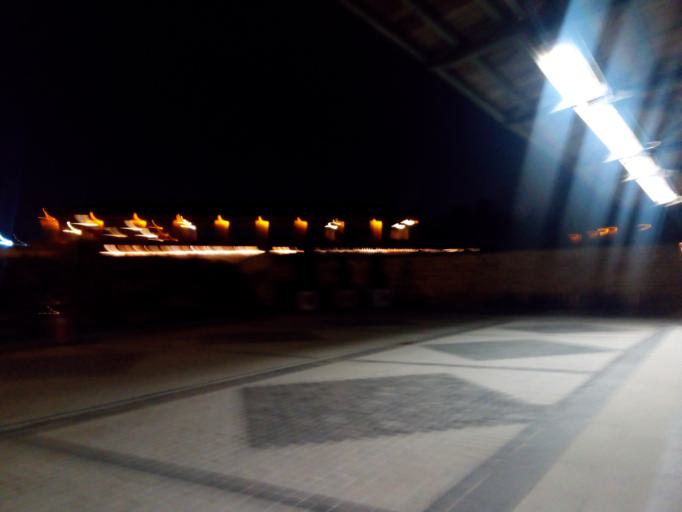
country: TR
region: Istanbul
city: Zeytinburnu
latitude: 41.0159
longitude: 28.9192
